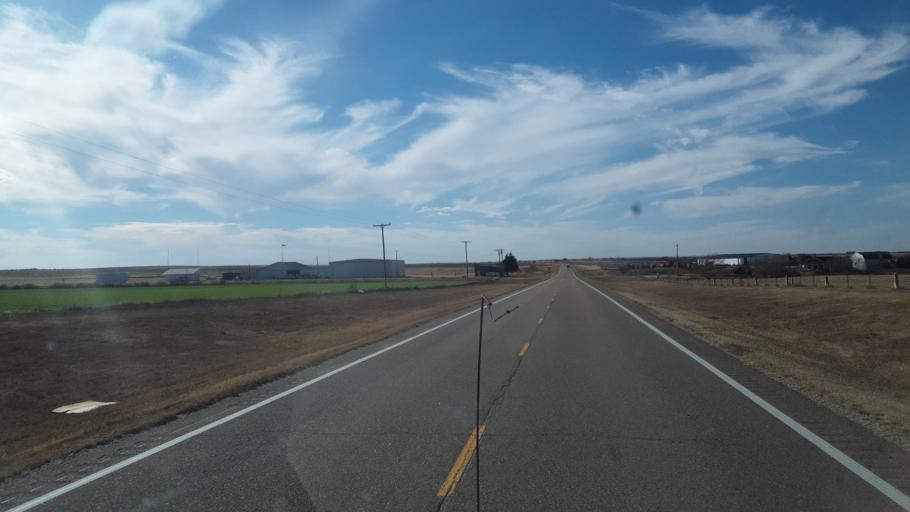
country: US
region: Kansas
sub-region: Edwards County
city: Kinsley
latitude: 38.1897
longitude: -99.5308
